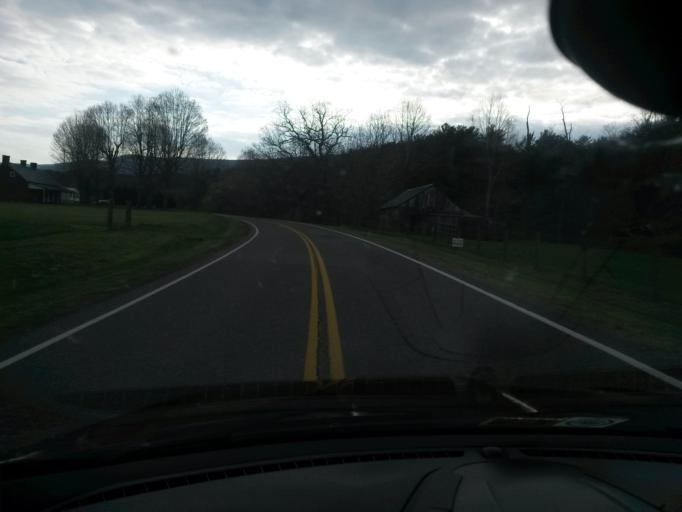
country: US
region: Virginia
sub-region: Alleghany County
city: Clifton Forge
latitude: 37.7935
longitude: -79.7157
